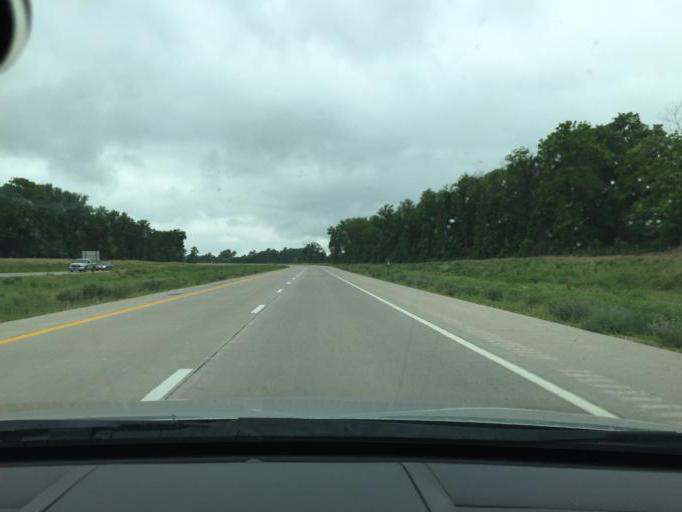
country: US
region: Kansas
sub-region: Reno County
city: Buhler
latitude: 38.1485
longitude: -97.8625
